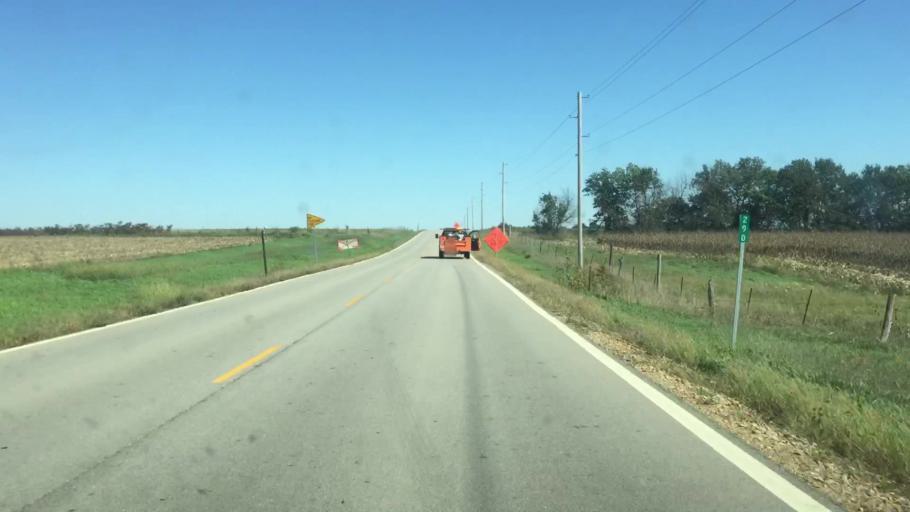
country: US
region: Kansas
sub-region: Jackson County
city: Holton
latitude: 39.5949
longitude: -95.6876
